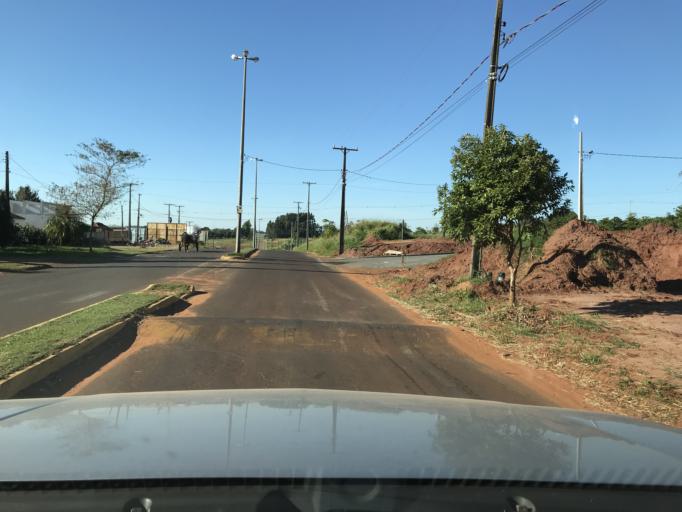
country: BR
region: Parana
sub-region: Ipora
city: Ipora
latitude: -24.0042
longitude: -53.6994
